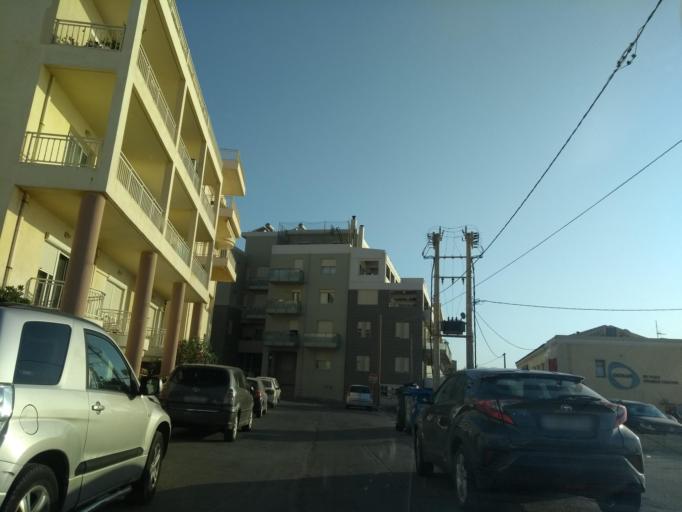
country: GR
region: Crete
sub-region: Nomos Rethymnis
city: Rethymno
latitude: 35.3662
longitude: 24.4661
